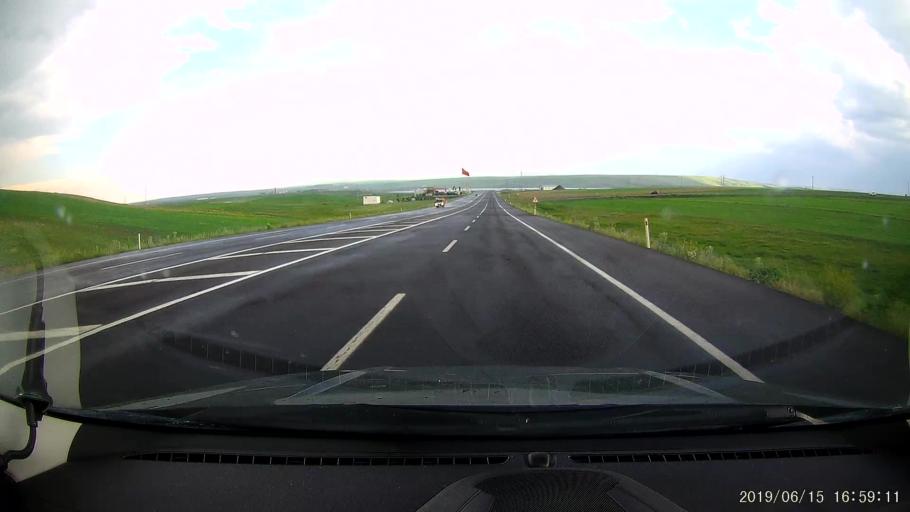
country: TR
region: Kars
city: Susuz
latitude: 40.7551
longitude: 43.1489
